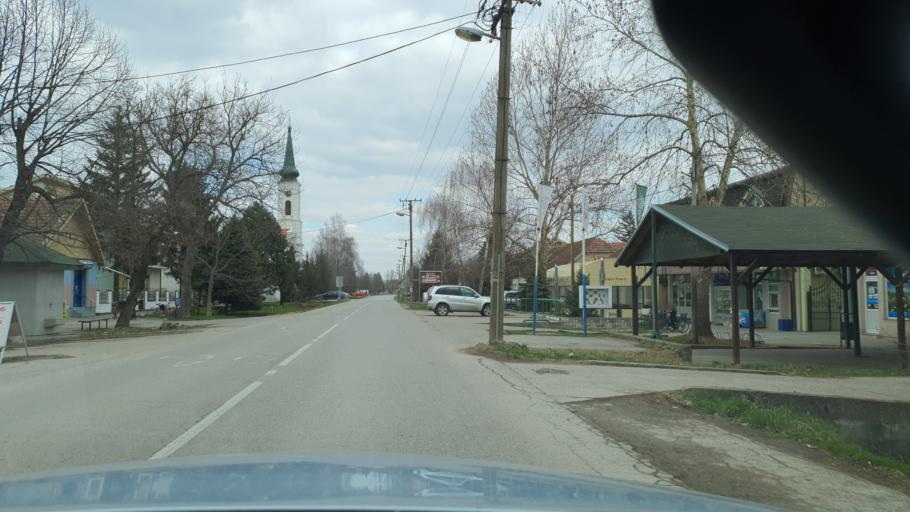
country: RS
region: Autonomna Pokrajina Vojvodina
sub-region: Juznobacki Okrug
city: Bac
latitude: 45.4101
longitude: 19.2997
